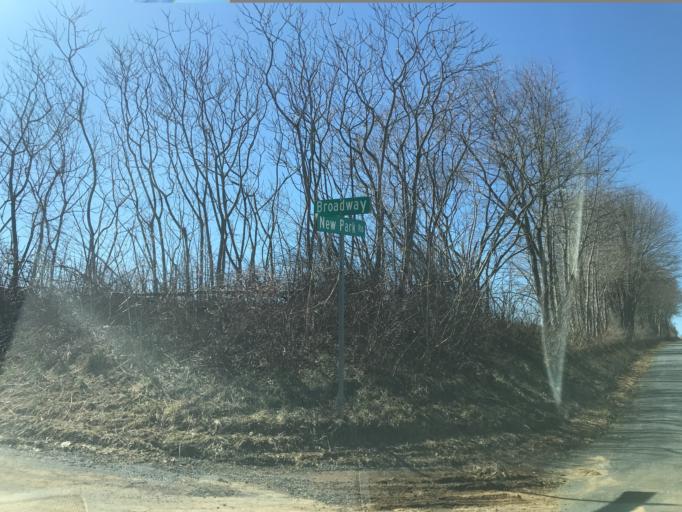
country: US
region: Pennsylvania
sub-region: York County
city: Stewartstown
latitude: 39.7122
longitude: -76.5273
